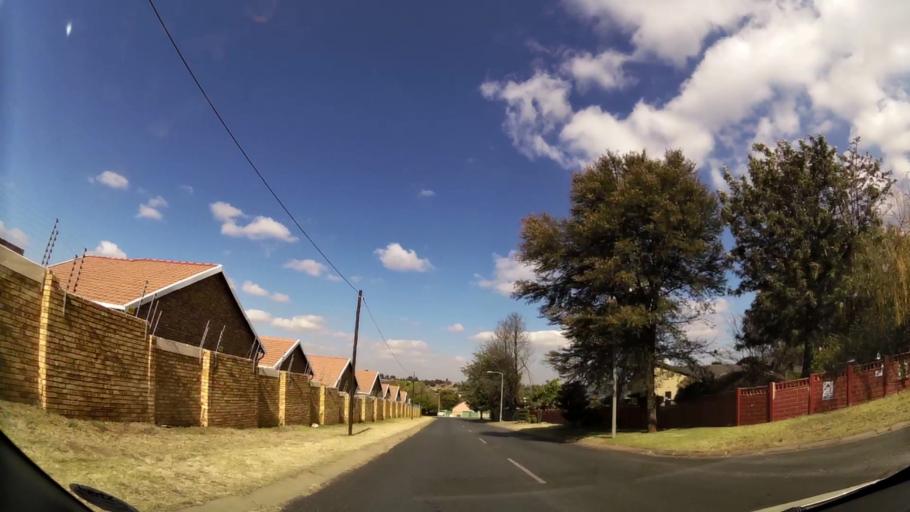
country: ZA
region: Gauteng
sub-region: City of Johannesburg Metropolitan Municipality
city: Roodepoort
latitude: -26.1188
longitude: 27.8382
